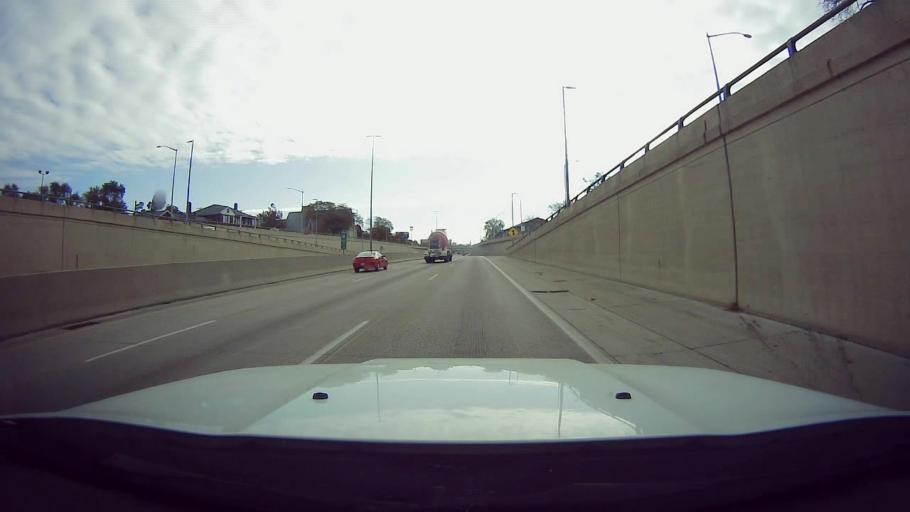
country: US
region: Michigan
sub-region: Oakland County
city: Oak Park
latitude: 42.4296
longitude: -83.1859
